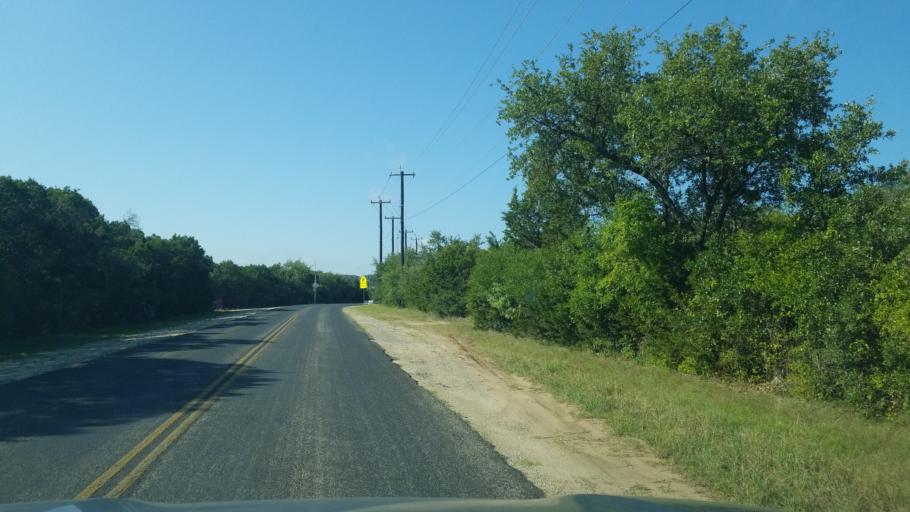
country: US
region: Texas
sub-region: Comal County
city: Bulverde
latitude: 29.7257
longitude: -98.4535
